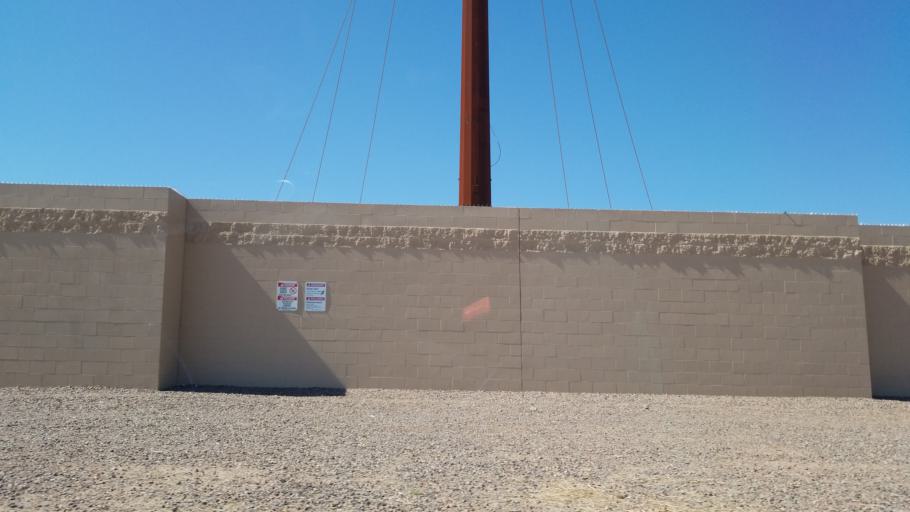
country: US
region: Arizona
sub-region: Maricopa County
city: Tolleson
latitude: 33.4742
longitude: -112.2293
